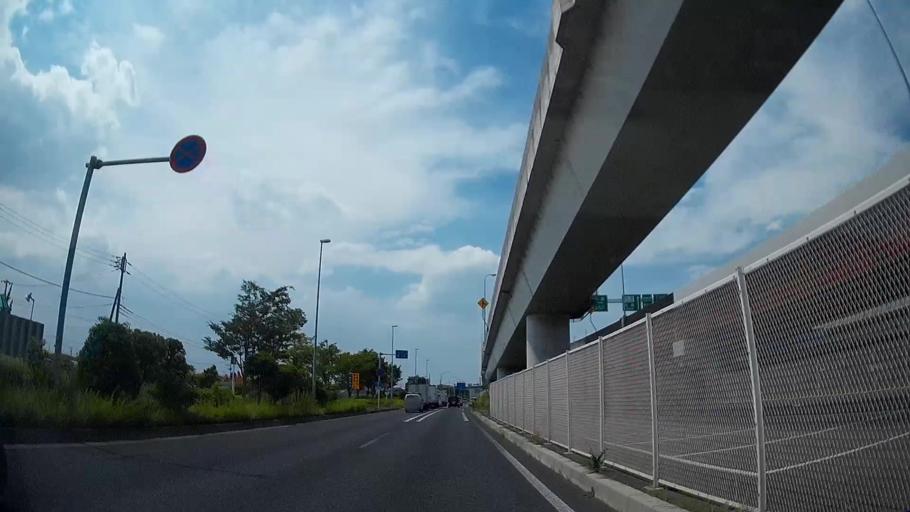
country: JP
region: Saitama
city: Yashio-shi
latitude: 35.8387
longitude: 139.8560
